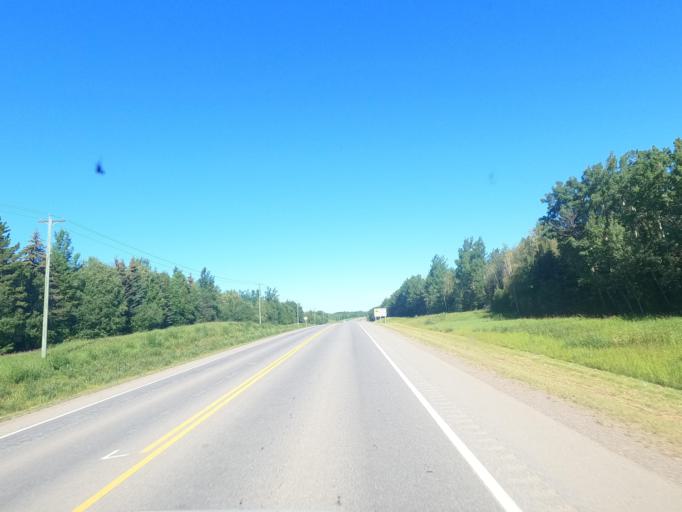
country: CA
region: British Columbia
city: Fort St. John
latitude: 56.6071
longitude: -121.4770
